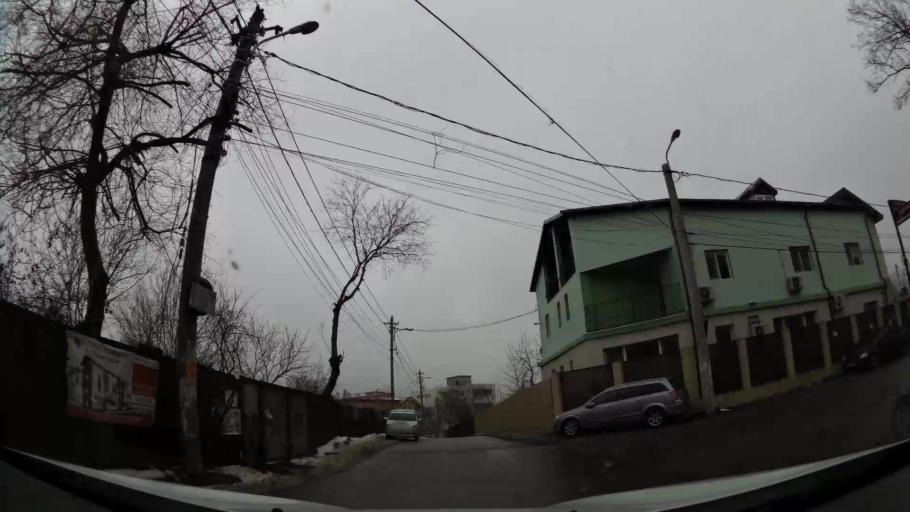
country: RO
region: Ilfov
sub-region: Comuna Popesti-Leordeni
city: Popesti-Leordeni
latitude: 44.4057
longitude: 26.1711
